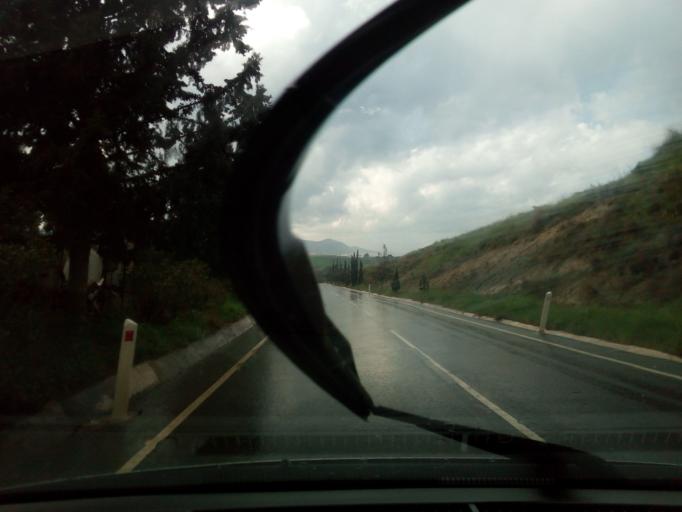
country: CY
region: Pafos
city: Polis
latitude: 35.0092
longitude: 32.4568
